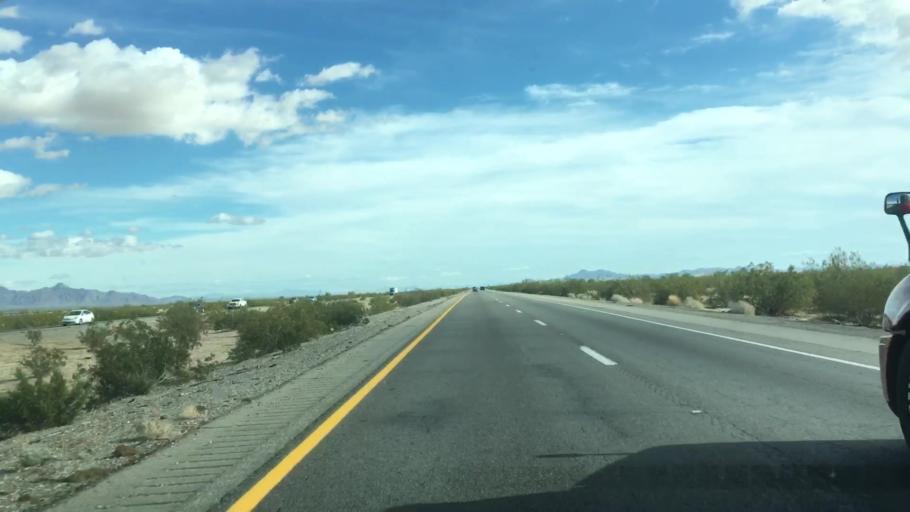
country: US
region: California
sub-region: Riverside County
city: Mesa Verde
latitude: 33.6272
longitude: -115.0613
